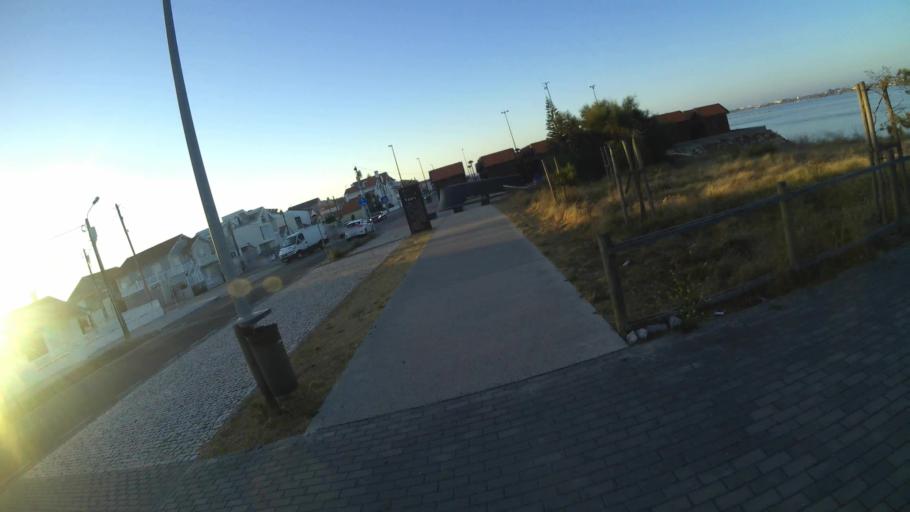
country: PT
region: Aveiro
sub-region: Ilhavo
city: Gafanha da Encarnacao
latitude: 40.6073
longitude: -8.7487
